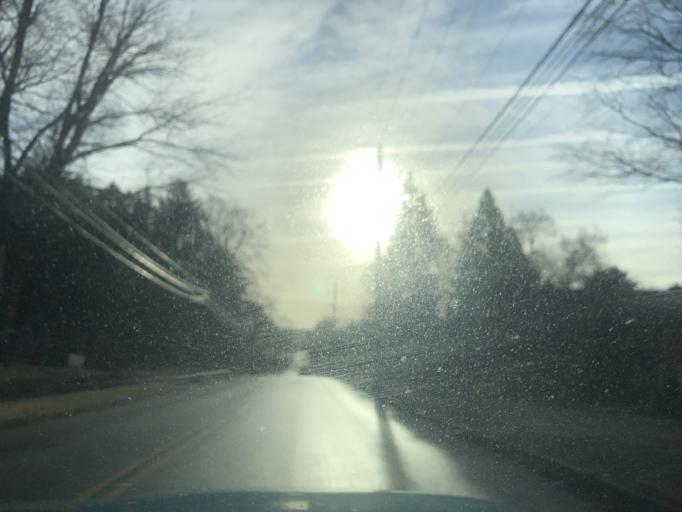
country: US
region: Pennsylvania
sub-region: Montgomery County
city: Fort Washington
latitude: 40.1466
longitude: -75.2013
